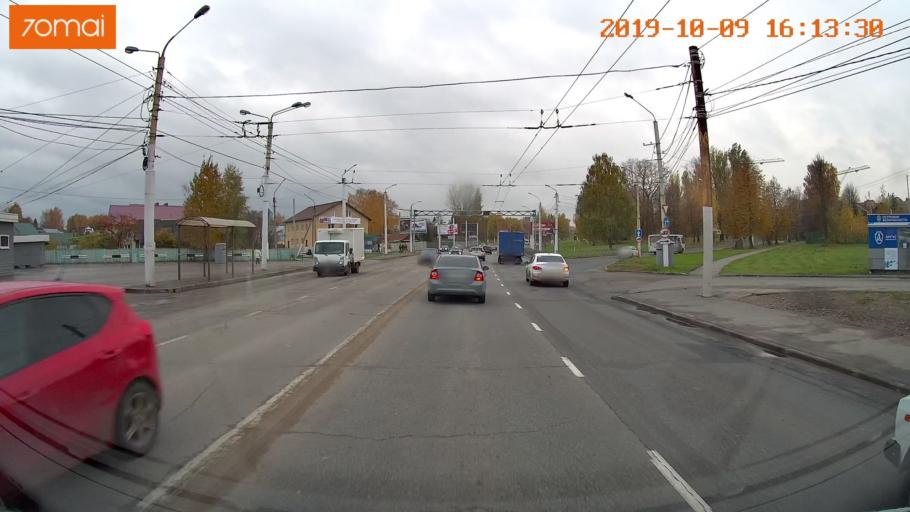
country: RU
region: Kostroma
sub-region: Kostromskoy Rayon
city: Kostroma
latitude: 57.7468
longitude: 40.9300
